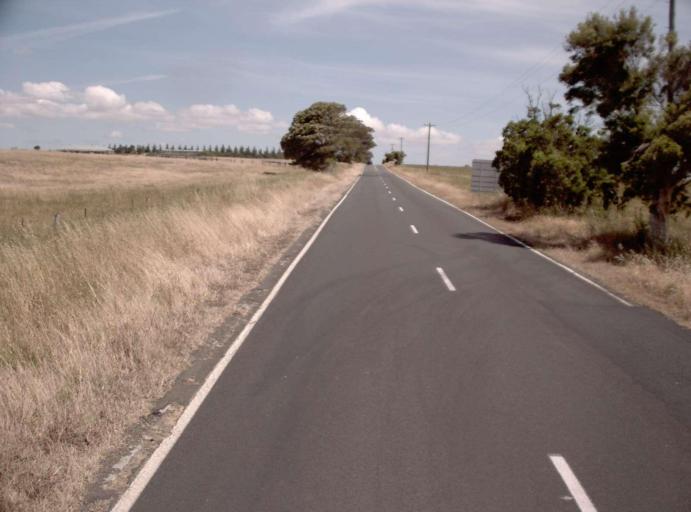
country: AU
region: Victoria
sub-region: Wellington
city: Heyfield
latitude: -38.1107
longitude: 146.8622
